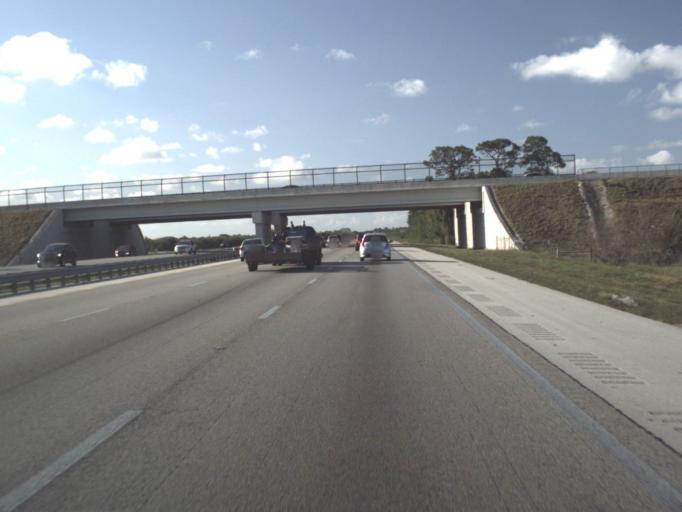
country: US
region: Florida
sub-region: Brevard County
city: Rockledge
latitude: 28.2654
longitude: -80.7285
